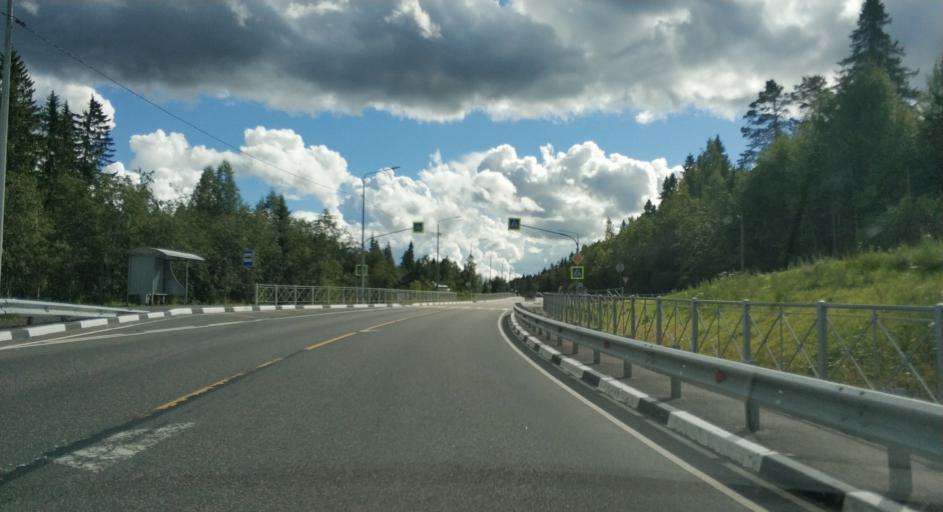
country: RU
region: Republic of Karelia
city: Ruskeala
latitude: 61.9306
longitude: 30.5969
